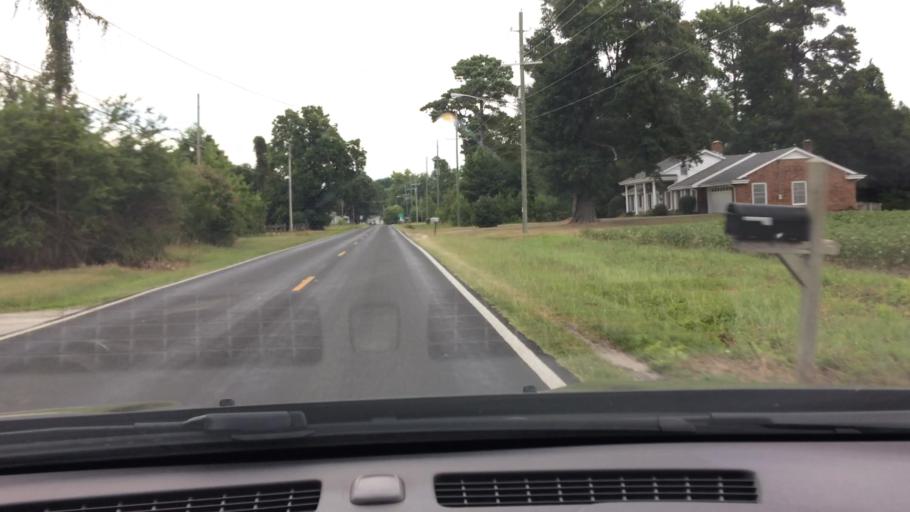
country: US
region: North Carolina
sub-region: Pitt County
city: Ayden
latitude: 35.4601
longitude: -77.4151
